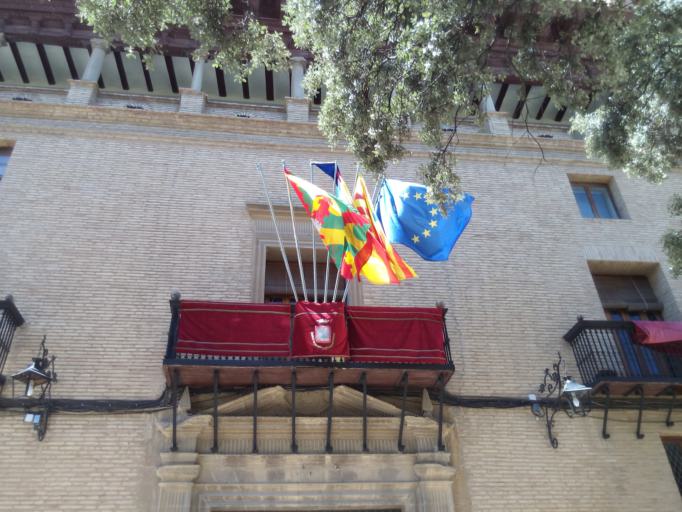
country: ES
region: Aragon
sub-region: Provincia de Huesca
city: Huesca
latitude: 42.1406
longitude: -0.4087
